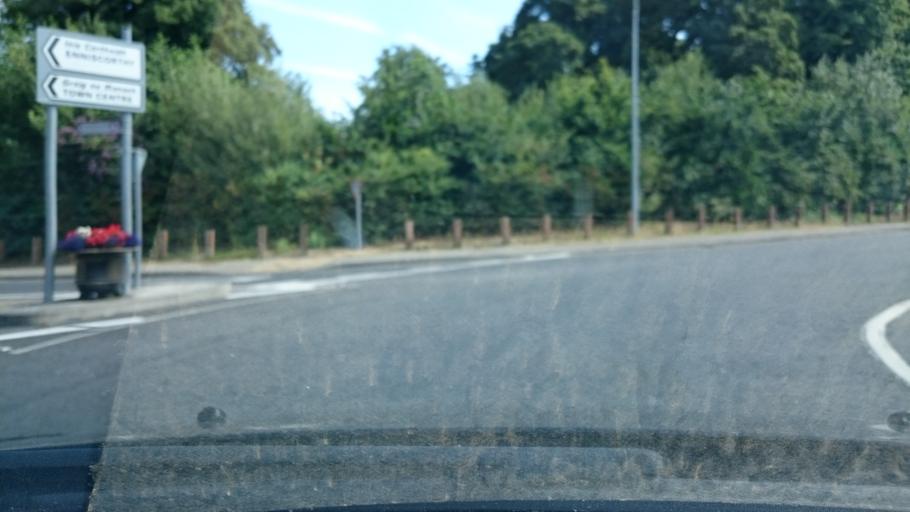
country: IE
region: Leinster
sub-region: Kilkenny
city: Graiguenamanagh
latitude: 52.5377
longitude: -6.9634
